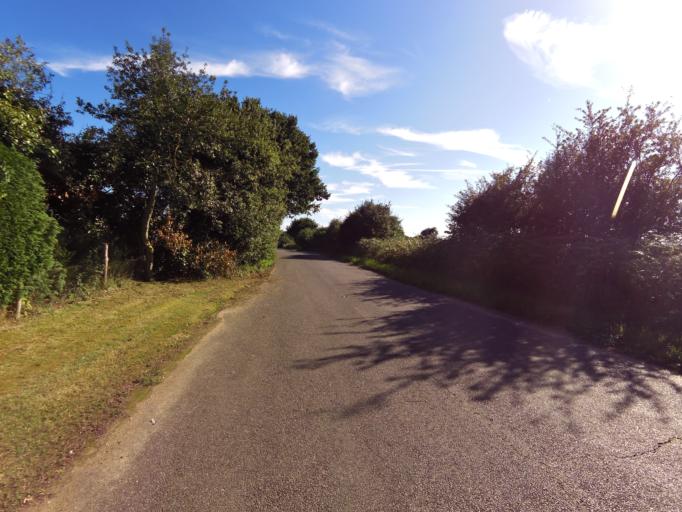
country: GB
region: England
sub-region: Suffolk
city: Kesgrave
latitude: 52.0496
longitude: 1.2782
